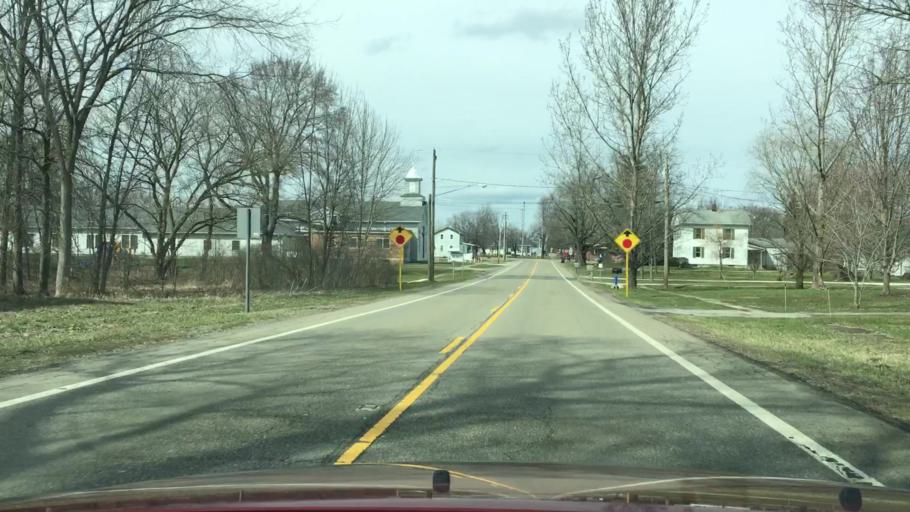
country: US
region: Ohio
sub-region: Mahoning County
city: Sebring
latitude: 41.0221
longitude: -81.0504
